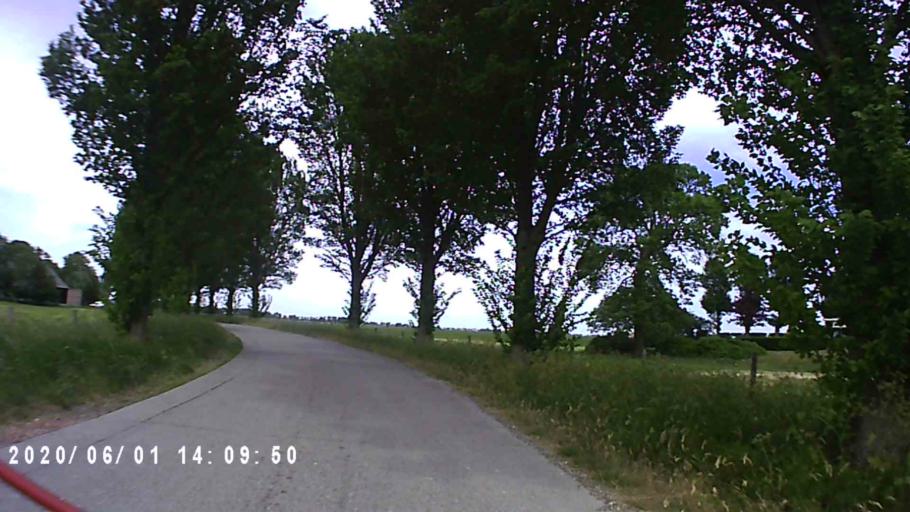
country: NL
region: Friesland
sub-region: Gemeente Littenseradiel
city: Winsum
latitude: 53.1222
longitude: 5.6478
